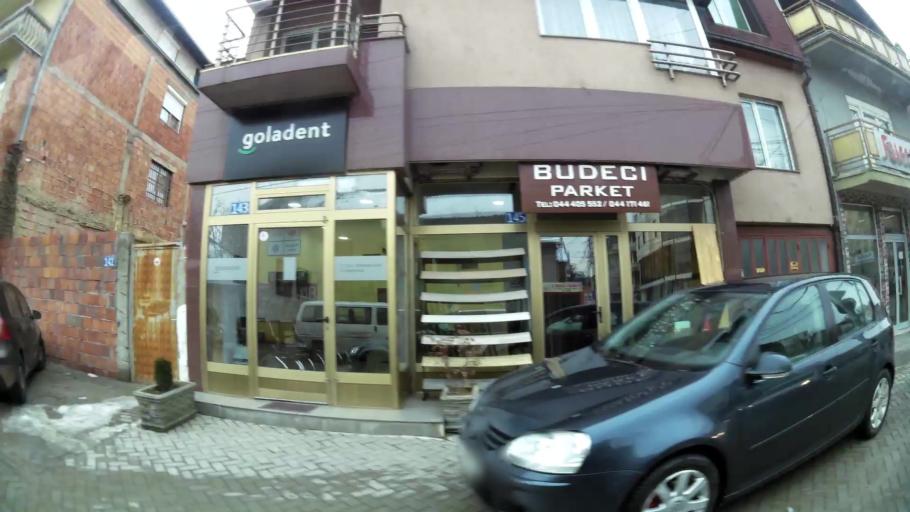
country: XK
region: Pristina
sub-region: Komuna e Prishtines
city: Pristina
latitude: 42.6671
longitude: 21.1603
